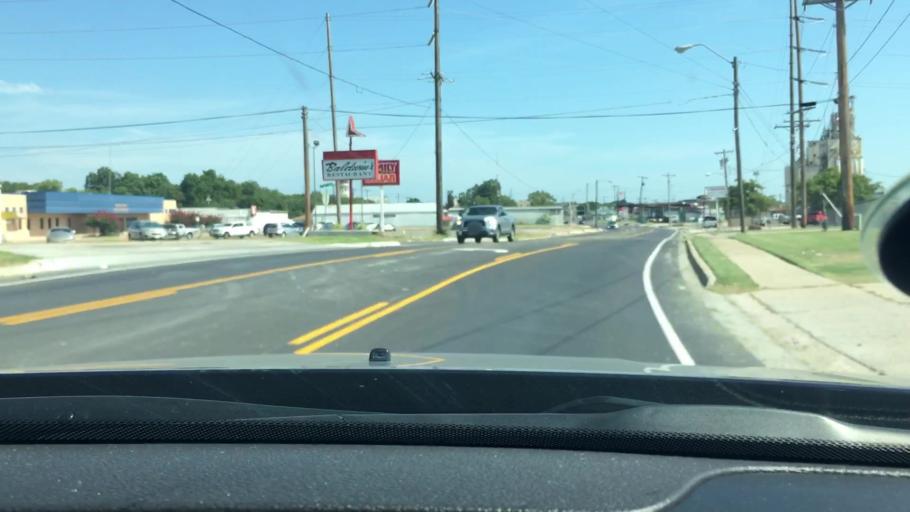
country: US
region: Oklahoma
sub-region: Carter County
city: Ardmore
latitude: 34.1658
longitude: -97.1312
